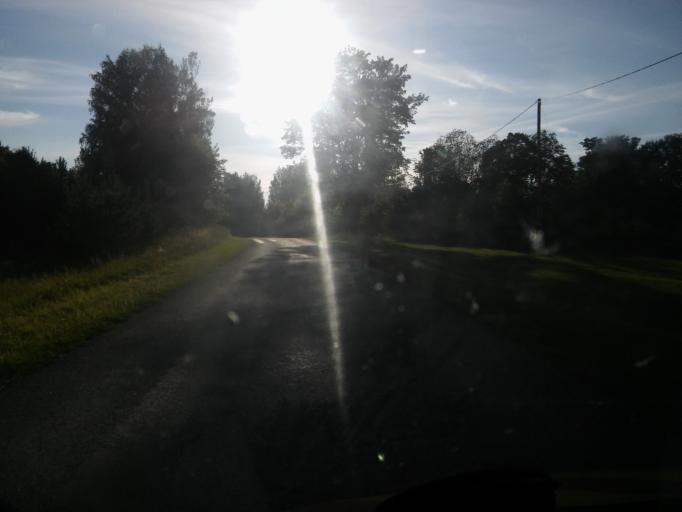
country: EE
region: Valgamaa
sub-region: Torva linn
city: Torva
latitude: 58.0807
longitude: 25.9699
